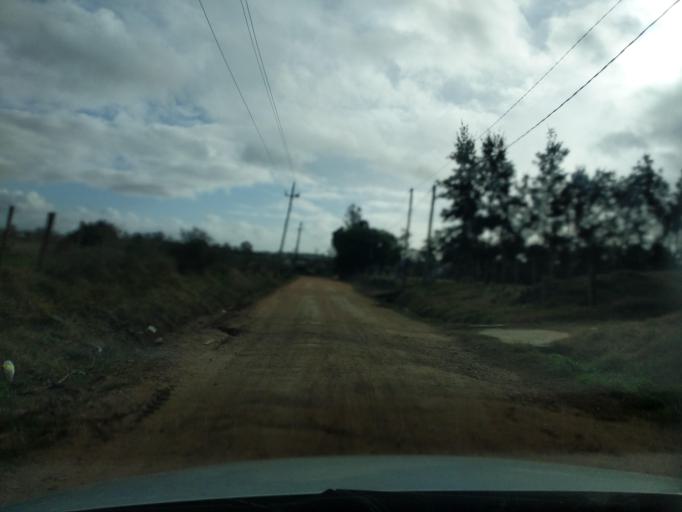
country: UY
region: Florida
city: Florida
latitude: -34.0696
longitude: -56.2202
